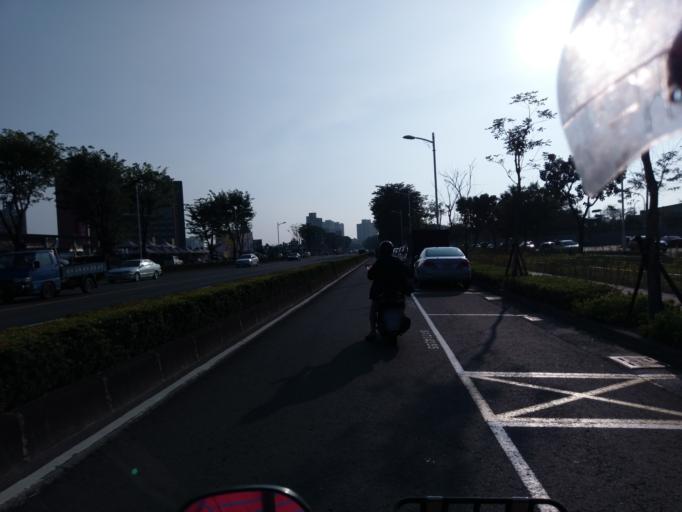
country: TW
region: Kaohsiung
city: Kaohsiung
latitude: 22.6007
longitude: 120.3211
